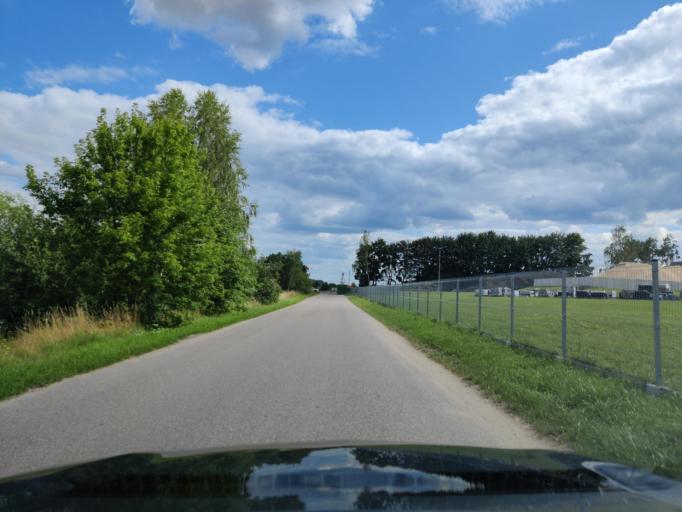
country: PL
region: Masovian Voivodeship
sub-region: Powiat sokolowski
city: Kosow Lacki
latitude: 52.5833
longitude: 22.1434
